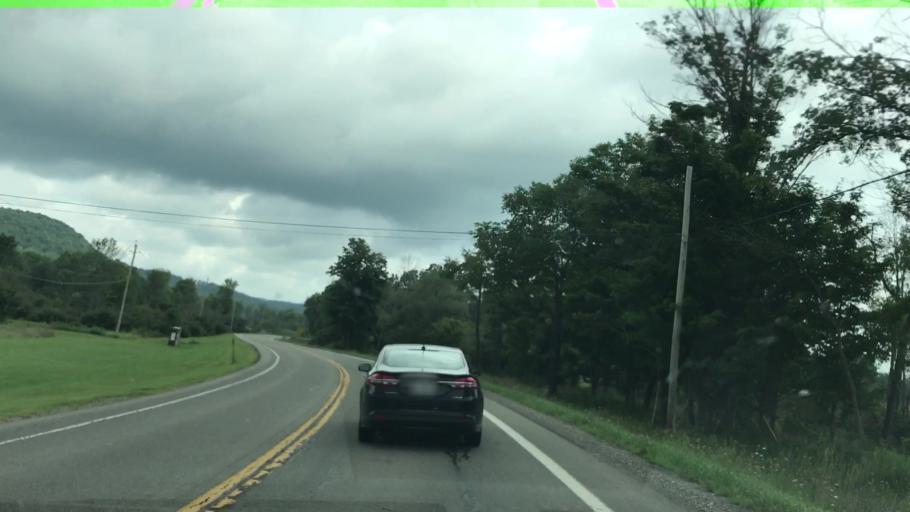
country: US
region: New York
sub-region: Steuben County
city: Bath
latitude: 42.4122
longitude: -77.3446
